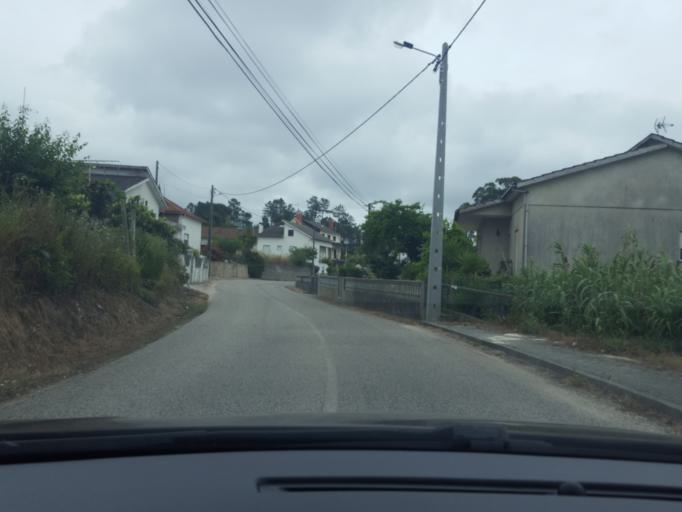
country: PT
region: Leiria
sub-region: Leiria
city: Caranguejeira
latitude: 39.7923
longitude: -8.7505
